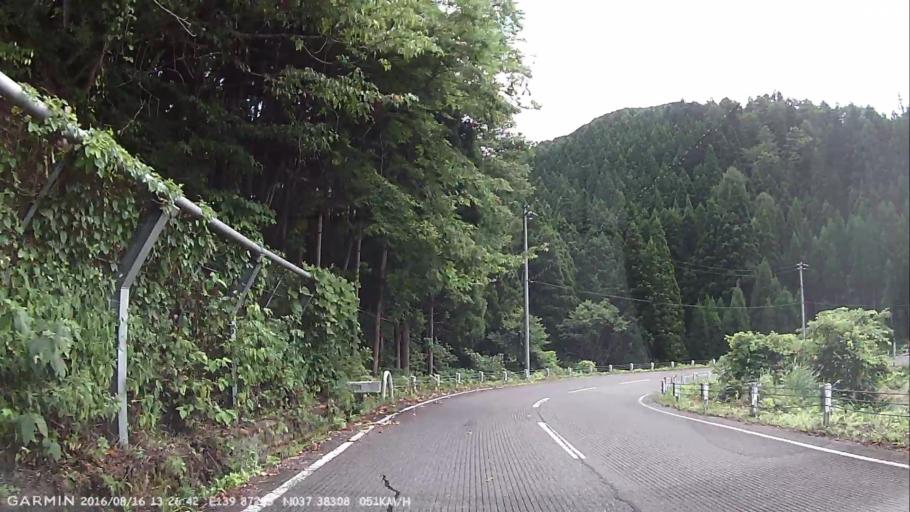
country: JP
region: Fukushima
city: Kitakata
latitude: 37.3831
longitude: 139.8729
